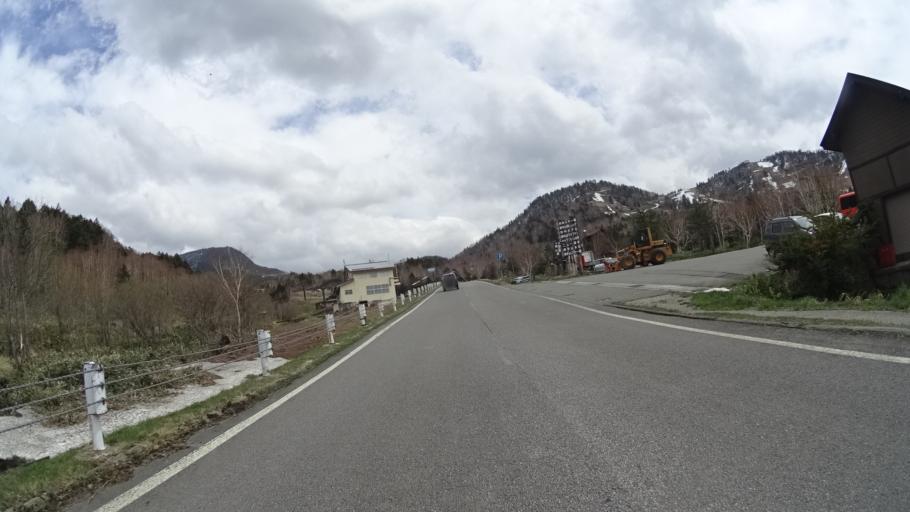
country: JP
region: Nagano
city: Nakano
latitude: 36.6845
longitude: 138.4985
